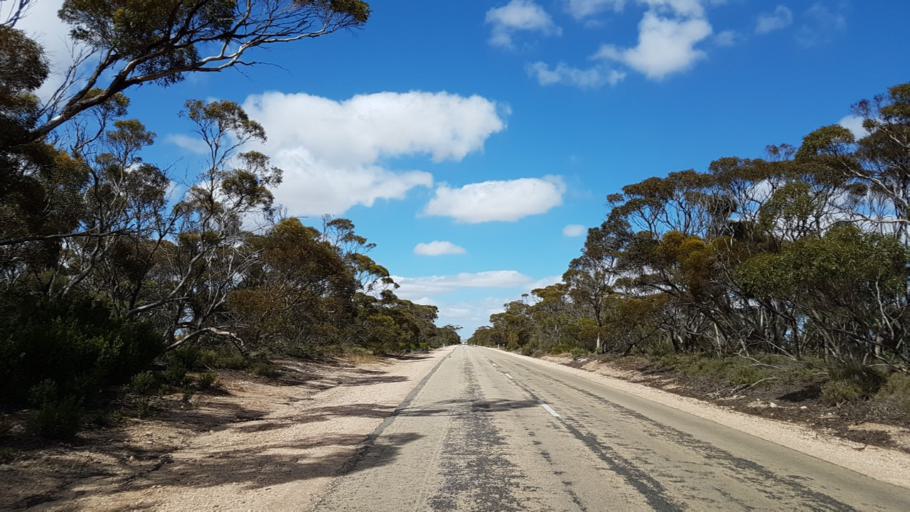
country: AU
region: South Australia
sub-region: Yorke Peninsula
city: Ardrossan
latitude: -34.5716
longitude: 137.8251
